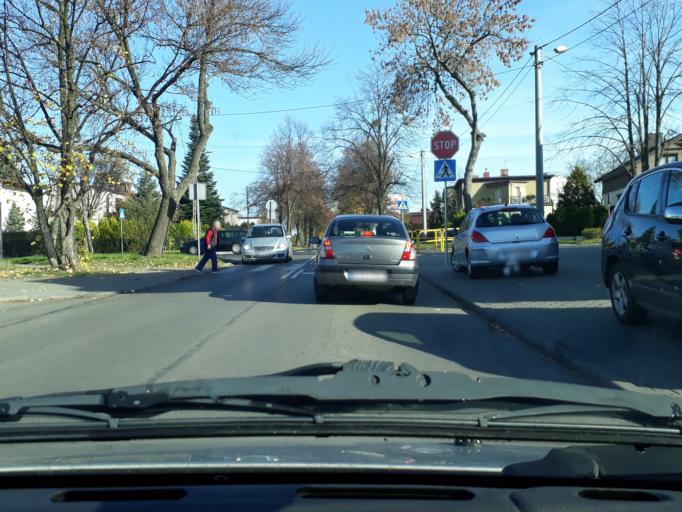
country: PL
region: Silesian Voivodeship
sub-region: Powiat tarnogorski
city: Tarnowskie Gory
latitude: 50.4340
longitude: 18.8670
